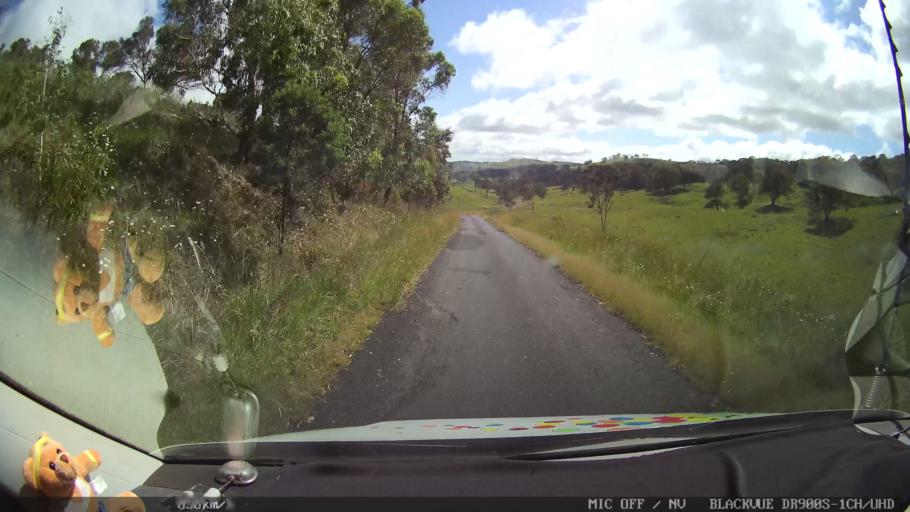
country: AU
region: New South Wales
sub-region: Guyra
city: Guyra
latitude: -30.0003
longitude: 151.6727
